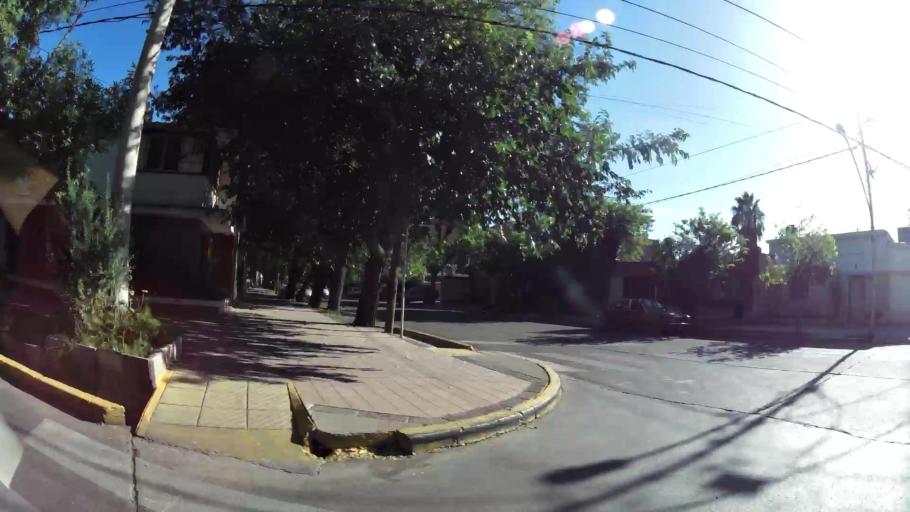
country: AR
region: Mendoza
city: Las Heras
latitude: -32.8664
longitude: -68.8399
